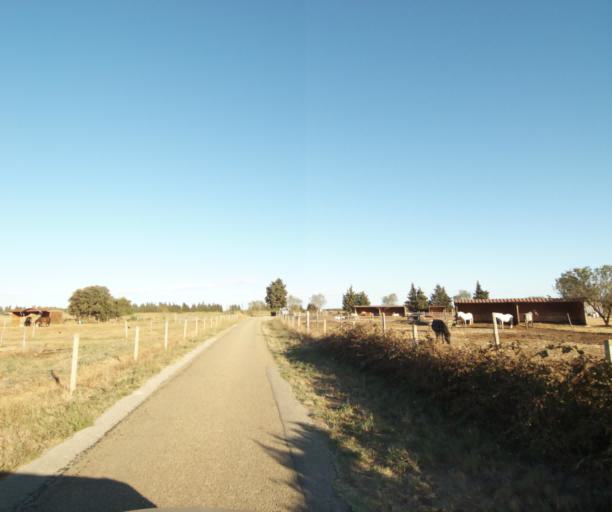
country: FR
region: Languedoc-Roussillon
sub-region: Departement du Gard
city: Garons
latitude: 43.7815
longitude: 4.4567
